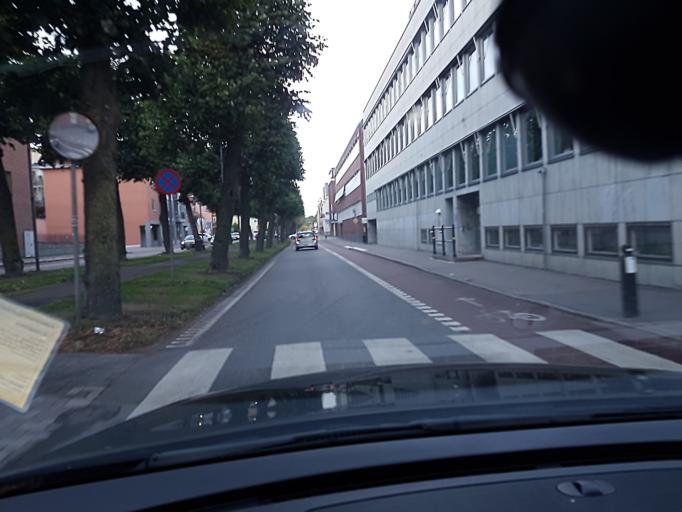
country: SE
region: Kronoberg
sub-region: Vaxjo Kommun
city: Vaexjoe
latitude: 56.8792
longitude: 14.8115
